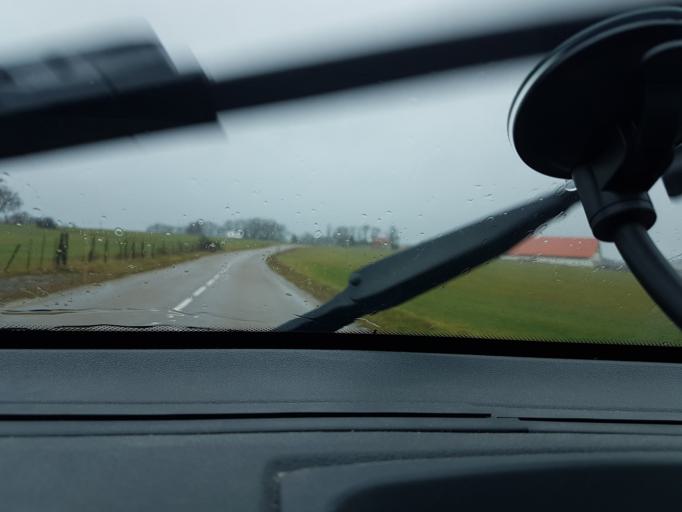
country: FR
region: Franche-Comte
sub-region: Departement du Doubs
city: Valdahon
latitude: 47.1243
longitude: 6.3635
